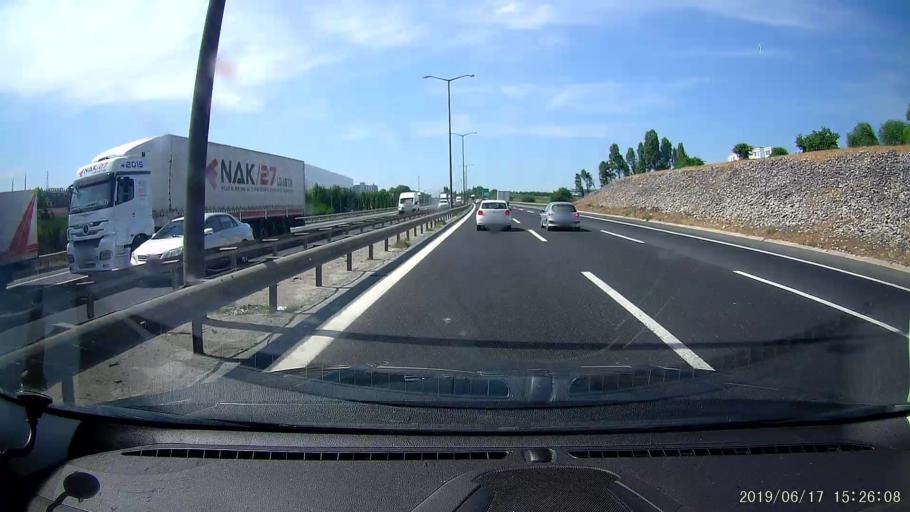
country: TR
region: Istanbul
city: Esenyurt
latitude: 41.0733
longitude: 28.6476
